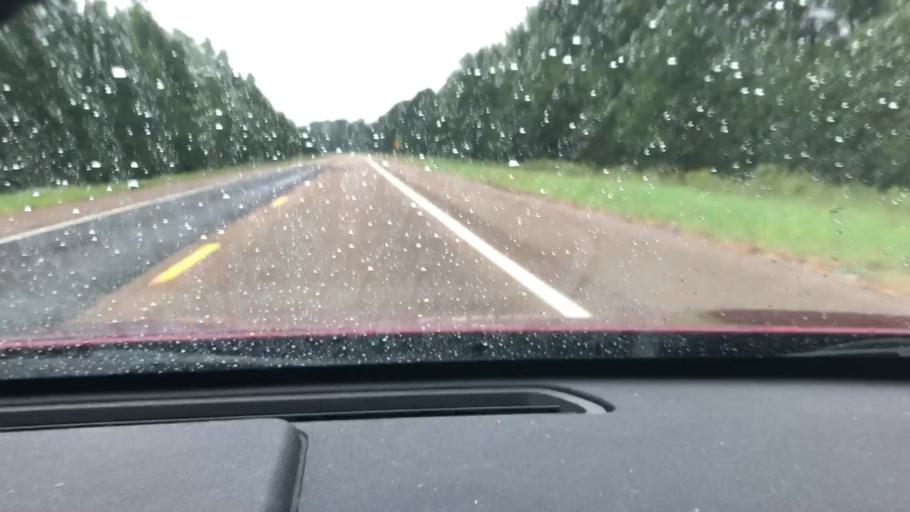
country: US
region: Arkansas
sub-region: Columbia County
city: Magnolia
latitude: 33.3020
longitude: -93.2685
